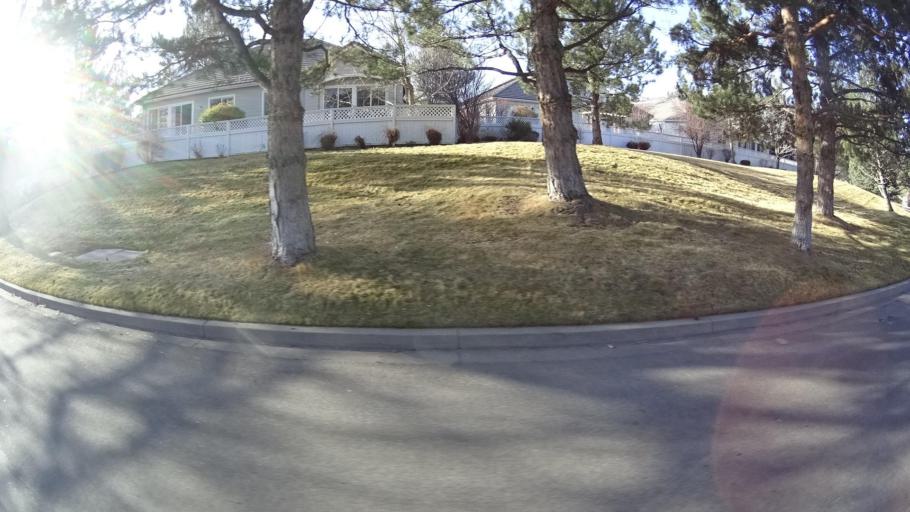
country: US
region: Nevada
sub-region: Washoe County
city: Reno
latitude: 39.5013
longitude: -119.8609
